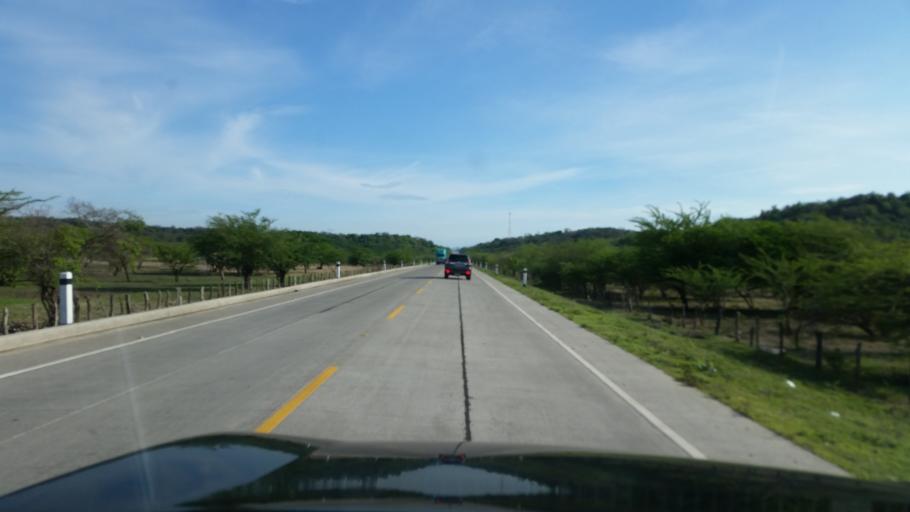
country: NI
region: Leon
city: Nagarote
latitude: 12.1921
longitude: -86.6774
